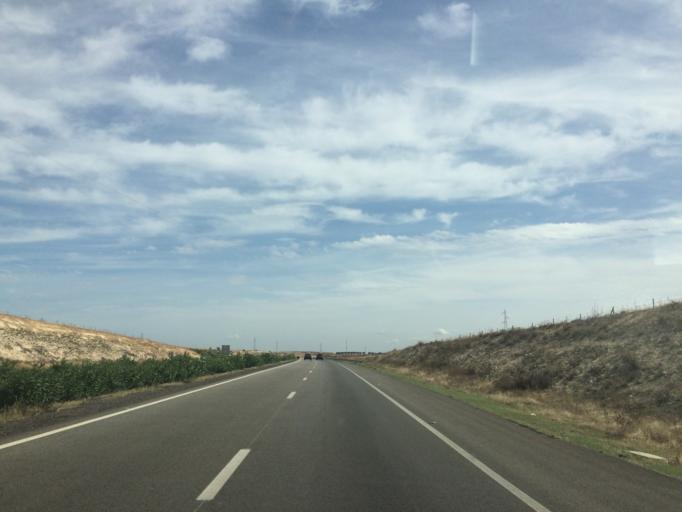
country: MA
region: Meknes-Tafilalet
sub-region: Meknes
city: Meknes
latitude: 33.8848
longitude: -5.7443
